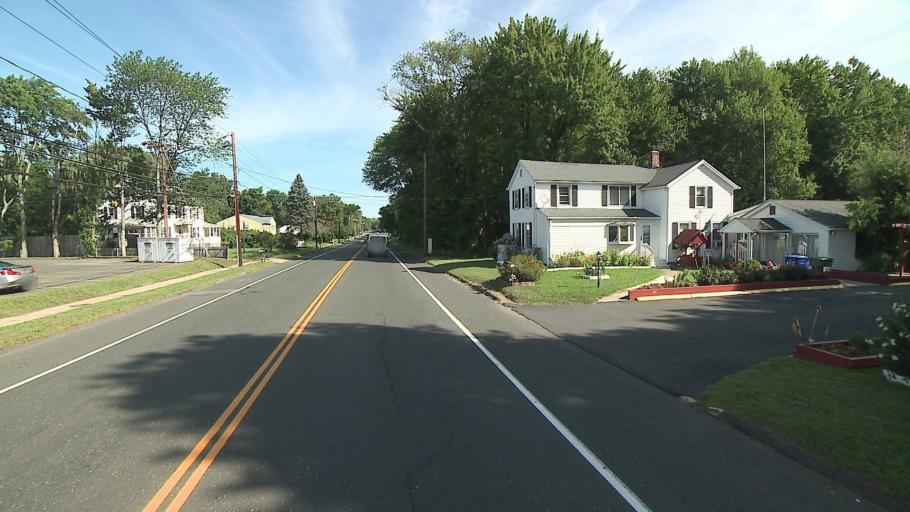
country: US
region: Connecticut
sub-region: Hartford County
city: Blue Hills
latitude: 41.8237
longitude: -72.6963
